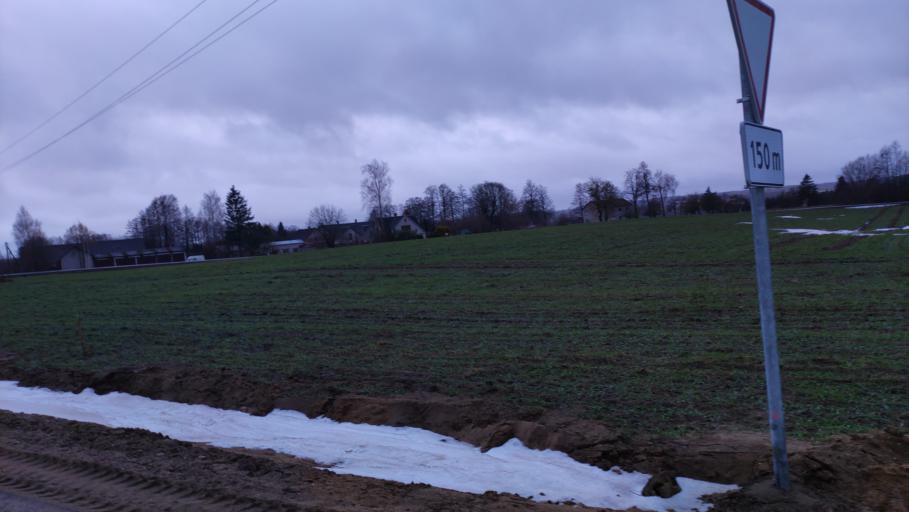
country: LT
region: Alytaus apskritis
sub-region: Alytus
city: Alytus
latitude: 54.4060
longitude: 23.9515
